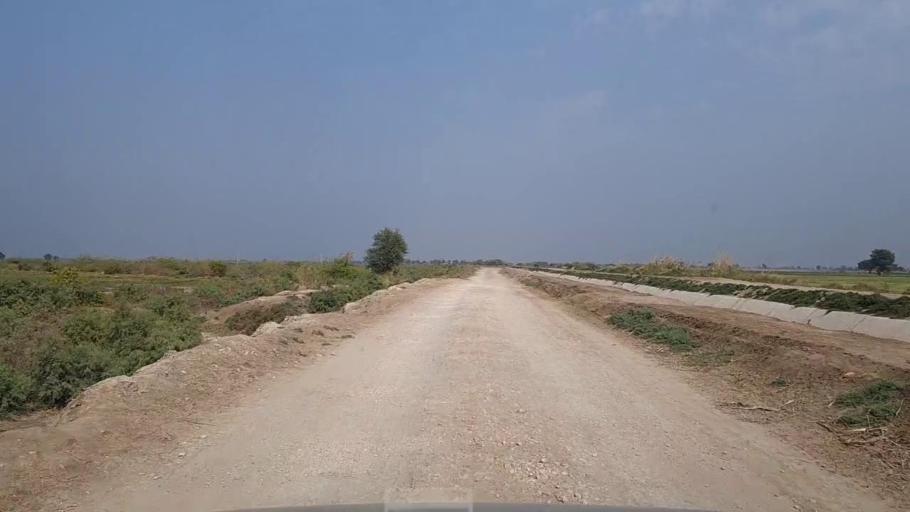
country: PK
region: Sindh
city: Mirwah Gorchani
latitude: 25.3959
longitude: 69.0713
